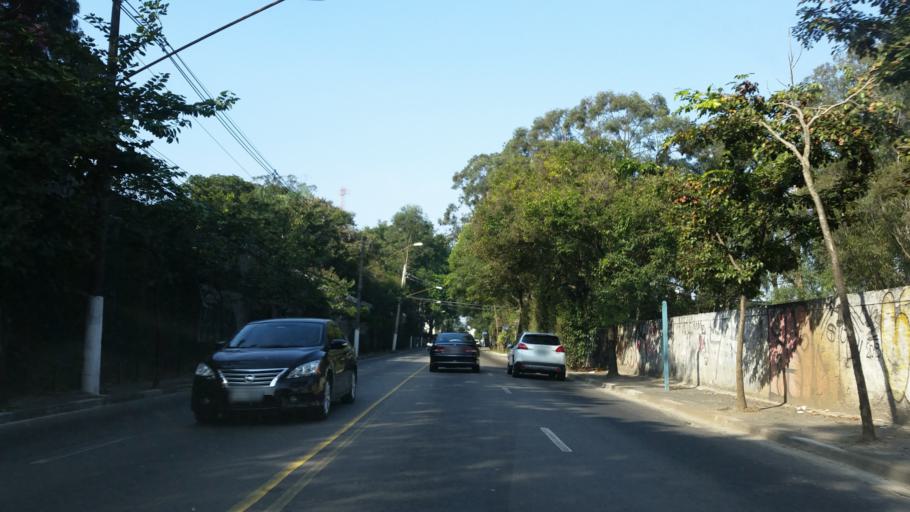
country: BR
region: Sao Paulo
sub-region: Diadema
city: Diadema
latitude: -23.6515
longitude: -46.6842
